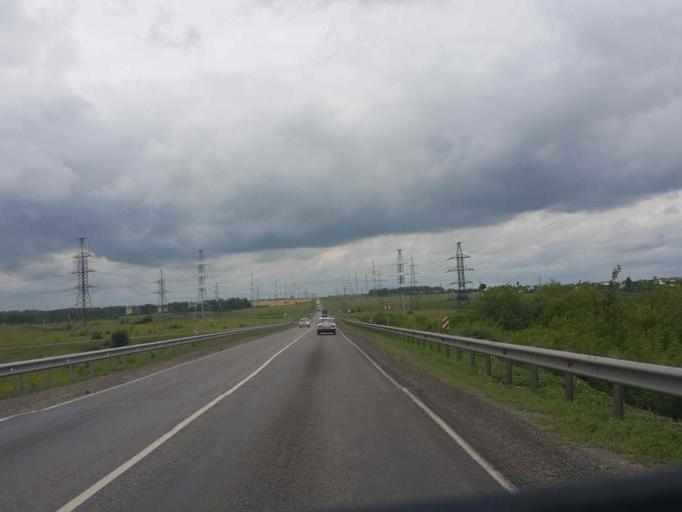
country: RU
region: Tambov
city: Komsomolets
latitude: 52.7673
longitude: 41.3257
